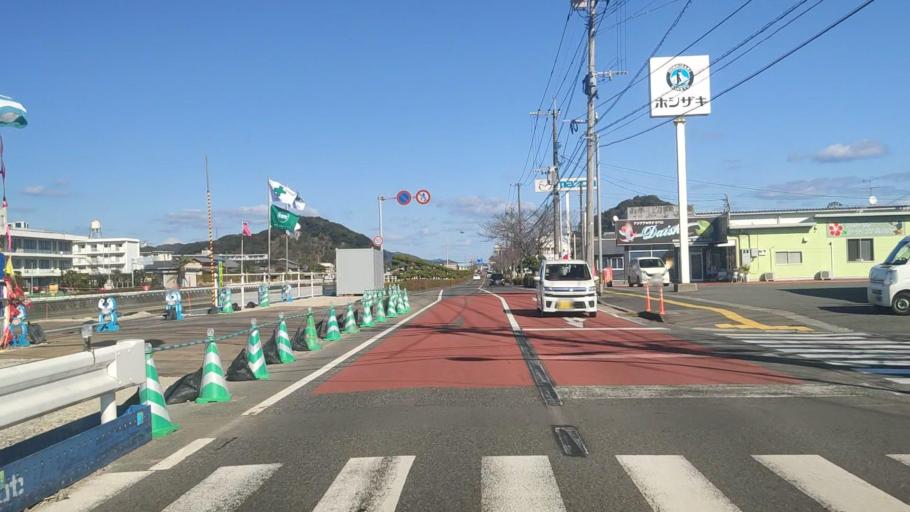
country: JP
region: Oita
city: Saiki
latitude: 32.9523
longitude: 131.9062
